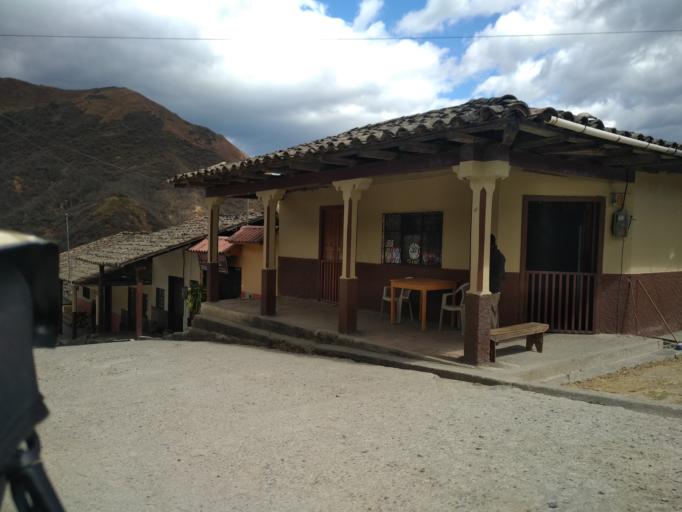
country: EC
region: Loja
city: Loja
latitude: -4.2431
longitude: -79.2219
